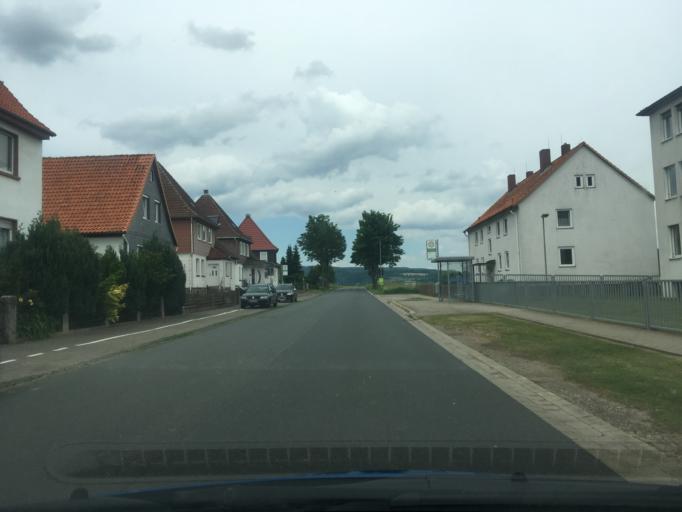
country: DE
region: Lower Saxony
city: Dassel
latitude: 51.7810
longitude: 9.6903
